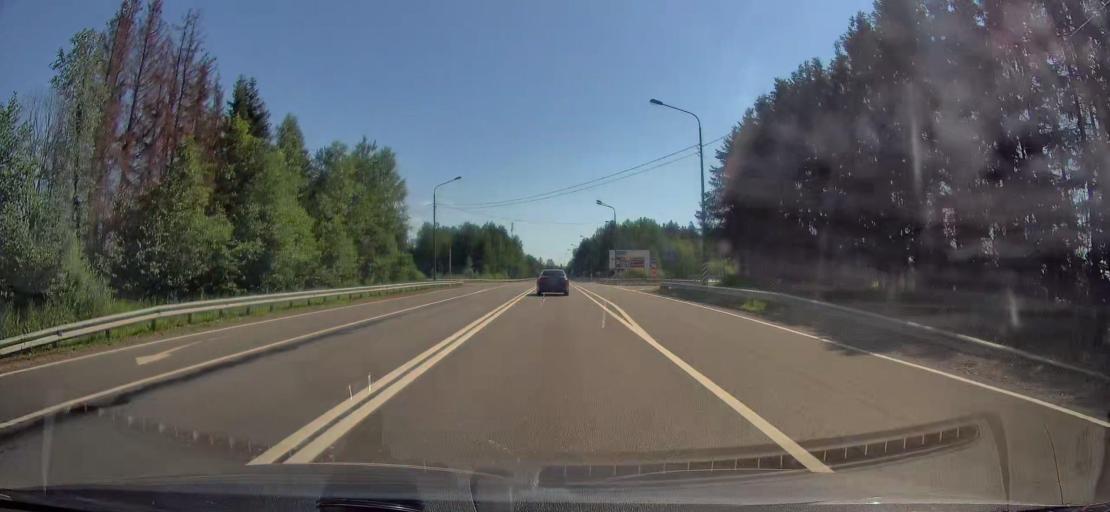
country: RU
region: Leningrad
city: Yefimovskiy
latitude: 59.3468
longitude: 34.8561
